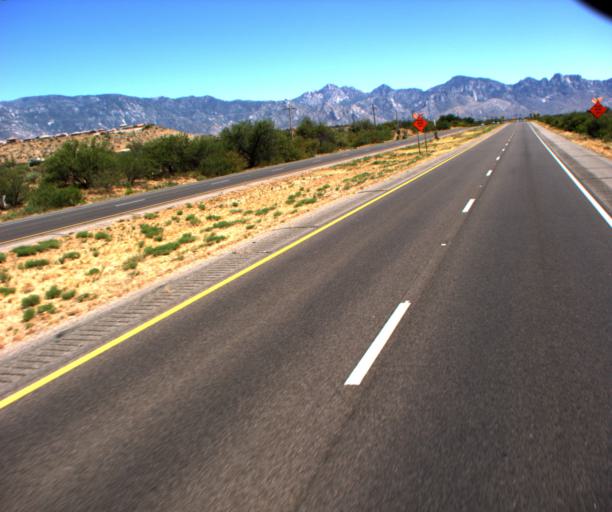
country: US
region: Arizona
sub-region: Pima County
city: Catalina
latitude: 32.5294
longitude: -110.9294
